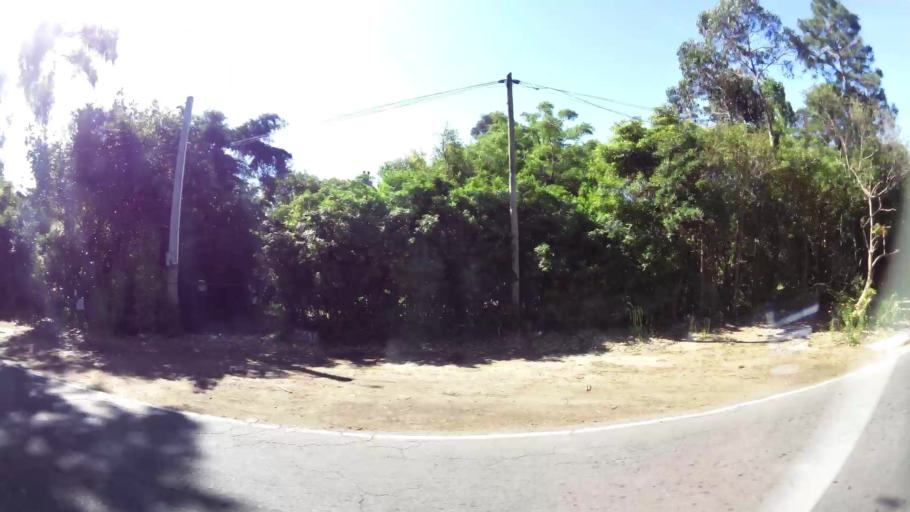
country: UY
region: Canelones
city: Barra de Carrasco
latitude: -34.8788
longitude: -56.0372
